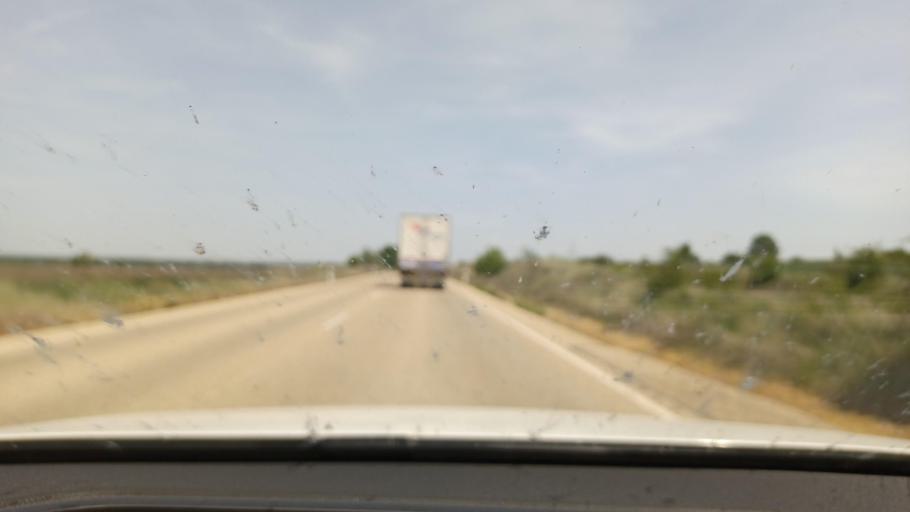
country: ES
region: Castille and Leon
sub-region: Provincia de Soria
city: Centenera de Andaluz
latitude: 41.4762
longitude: -2.7201
